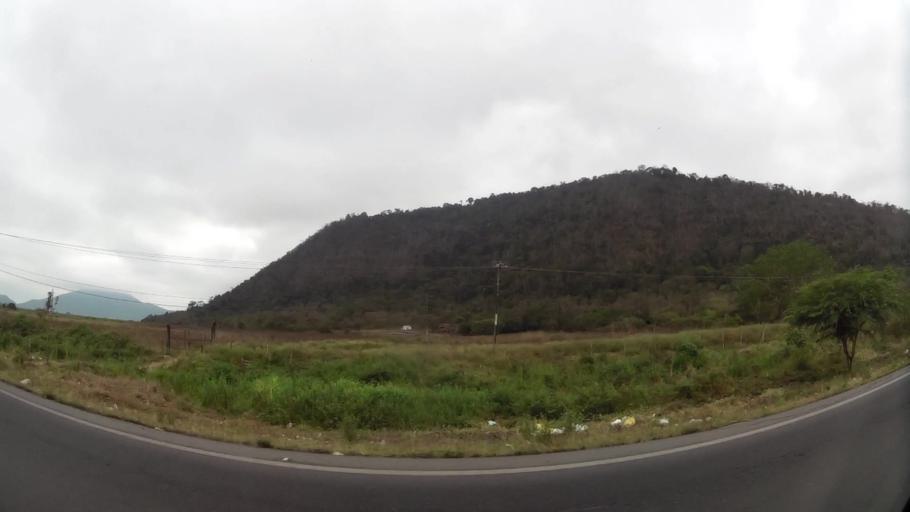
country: EC
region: Guayas
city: Naranjal
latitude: -2.4473
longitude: -79.6276
